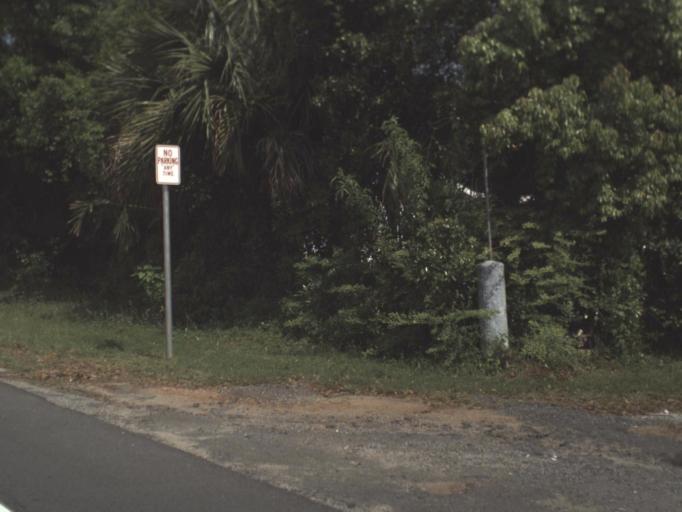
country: US
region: Florida
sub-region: Escambia County
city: Myrtle Grove
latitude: 30.4245
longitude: -87.2959
